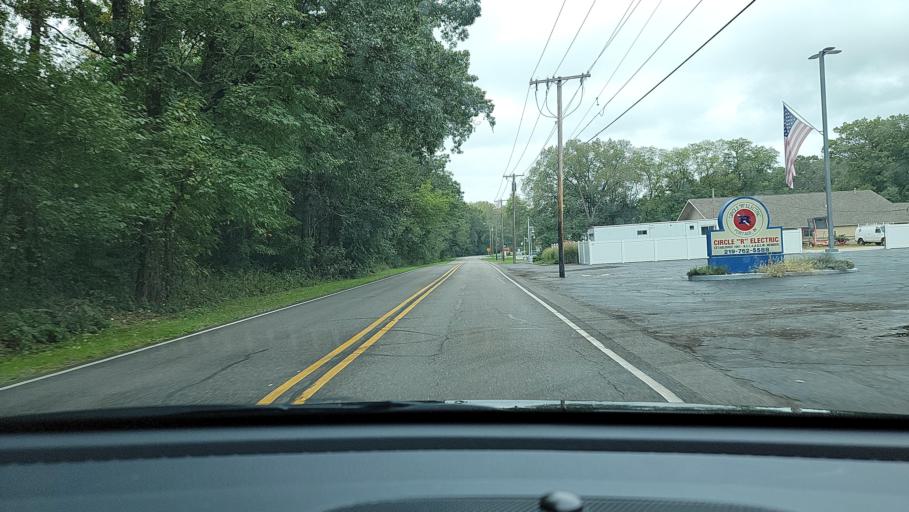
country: US
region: Indiana
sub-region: Porter County
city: Portage
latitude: 41.5759
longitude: -87.1930
